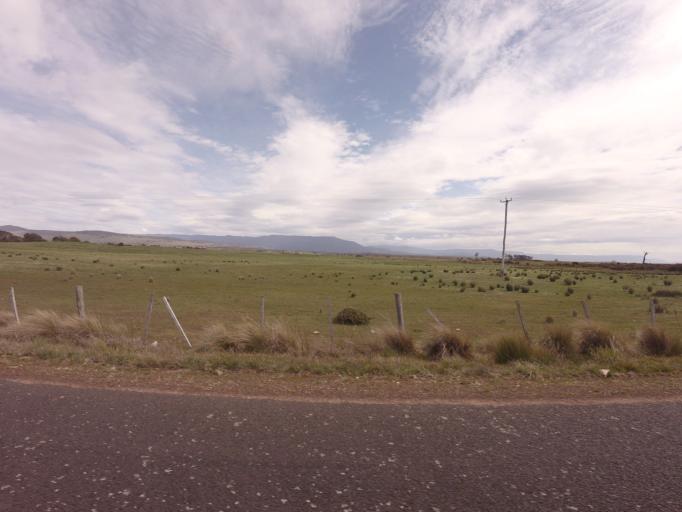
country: AU
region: Tasmania
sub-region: Northern Midlands
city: Evandale
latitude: -41.8440
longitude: 147.3352
